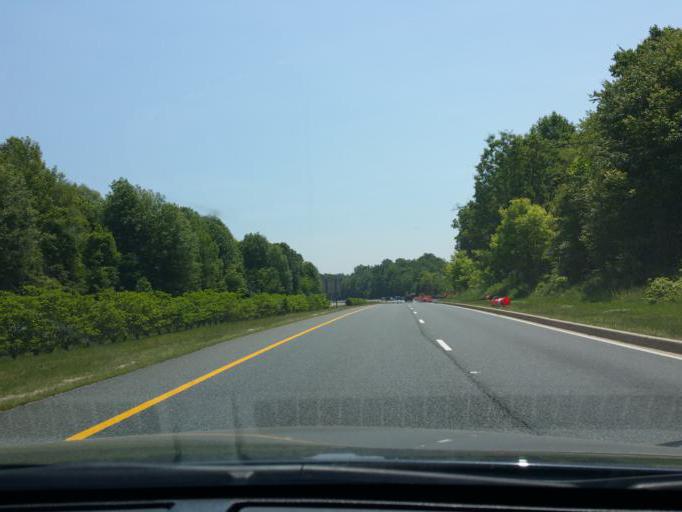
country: US
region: Maryland
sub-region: Baltimore County
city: Overlea
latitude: 39.3818
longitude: -76.4868
